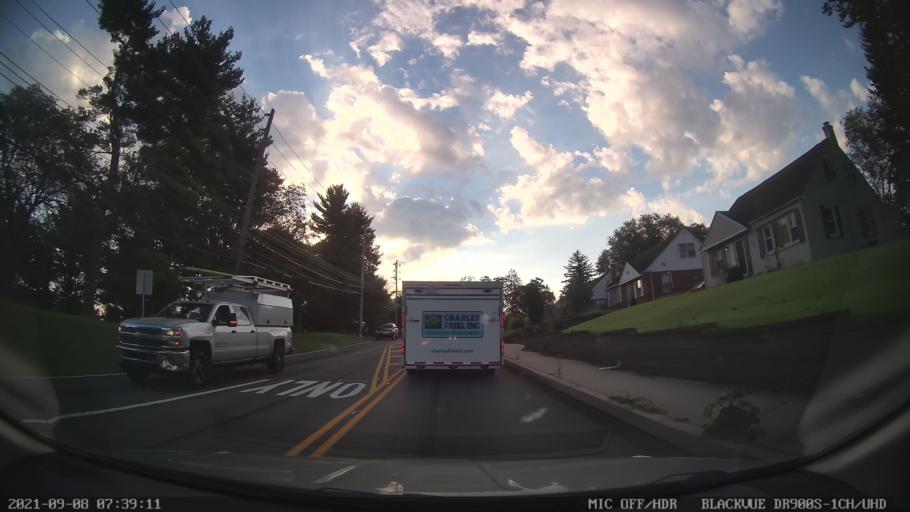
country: US
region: Pennsylvania
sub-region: Montgomery County
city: King of Prussia
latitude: 40.0824
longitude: -75.3799
